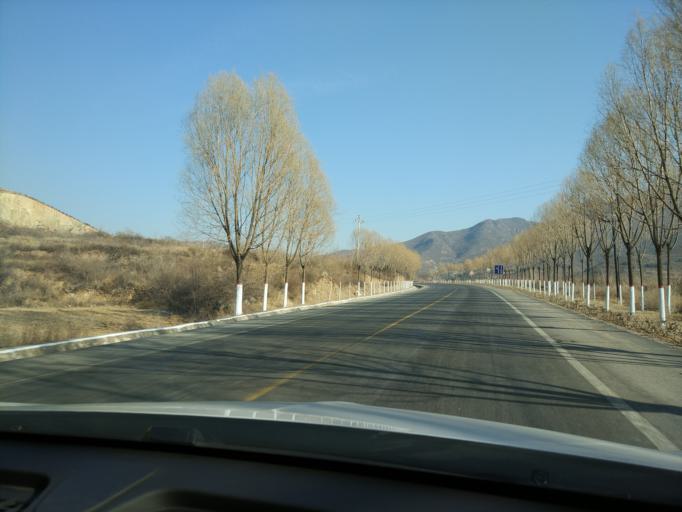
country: CN
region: Hebei
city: Shacheng
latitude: 40.5354
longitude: 115.6329
